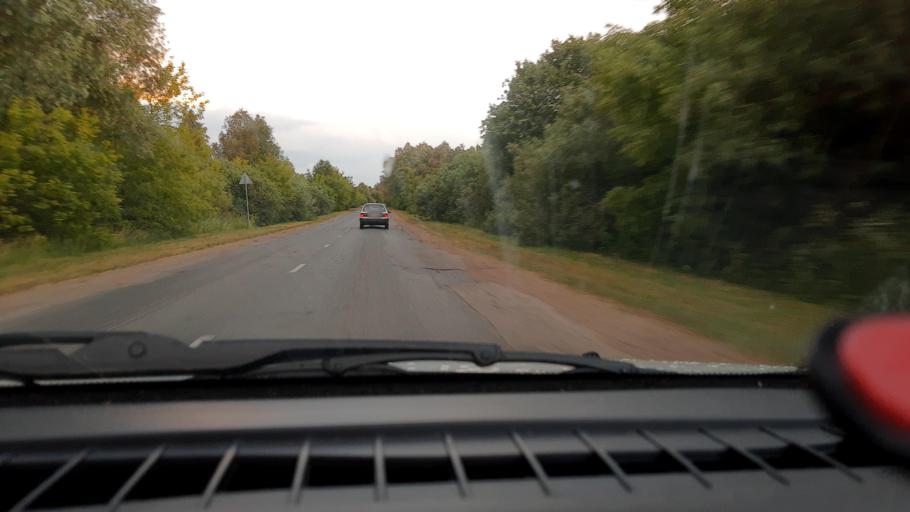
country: RU
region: Nizjnij Novgorod
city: Kstovo
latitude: 56.1319
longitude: 44.0724
